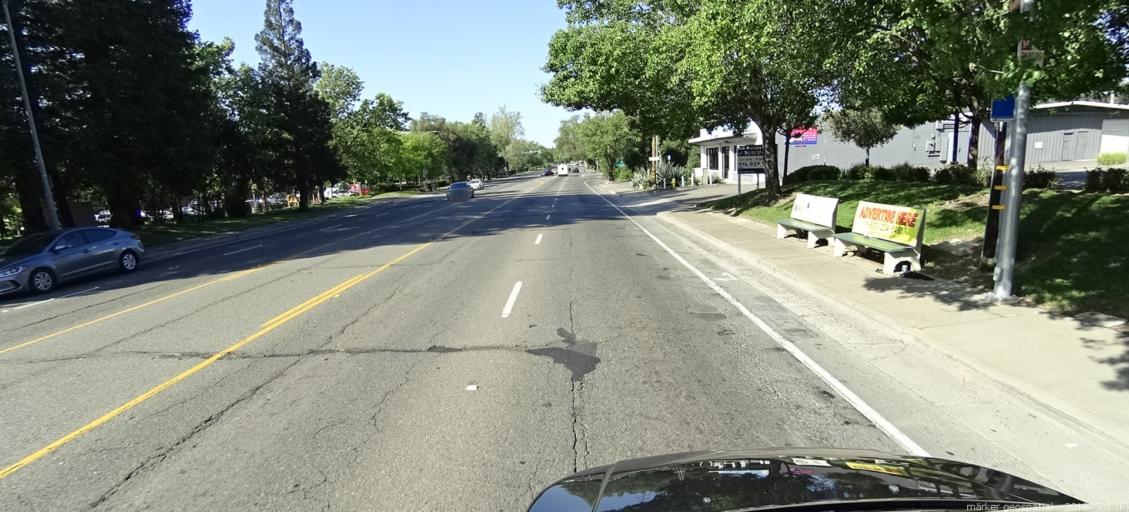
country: US
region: California
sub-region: Sacramento County
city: Foothill Farms
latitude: 38.6449
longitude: -121.3639
